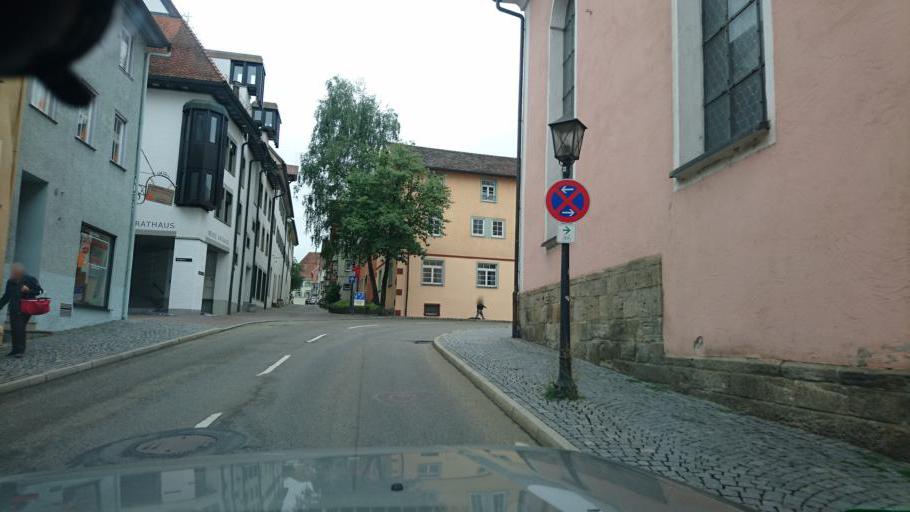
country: DE
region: Baden-Wuerttemberg
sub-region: Freiburg Region
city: Rottweil
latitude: 48.1688
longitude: 8.6264
